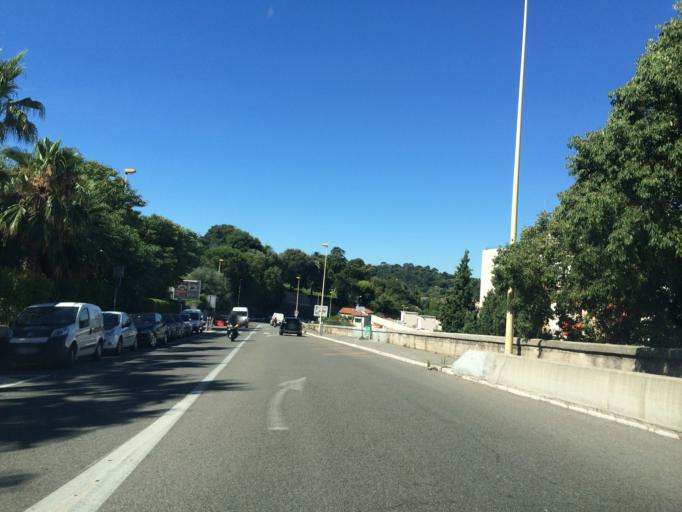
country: FR
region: Provence-Alpes-Cote d'Azur
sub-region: Departement des Alpes-Maritimes
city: Villefranche-sur-Mer
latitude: 43.7024
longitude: 7.2937
